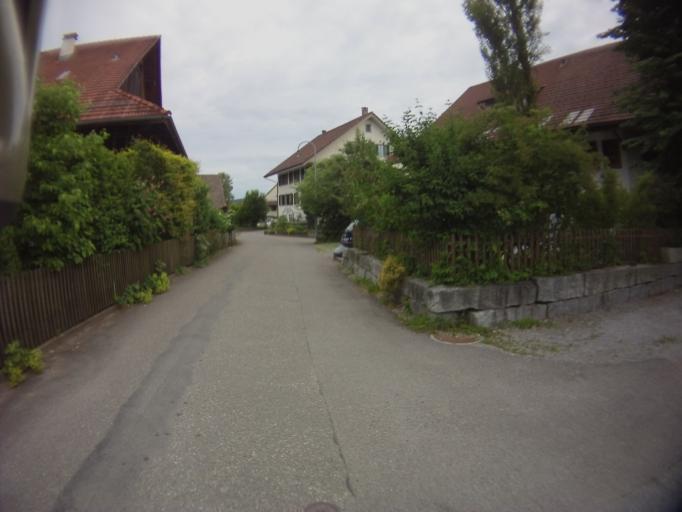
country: CH
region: Zurich
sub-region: Bezirk Affoltern
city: Mettmenstetten
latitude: 47.2400
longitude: 8.4966
